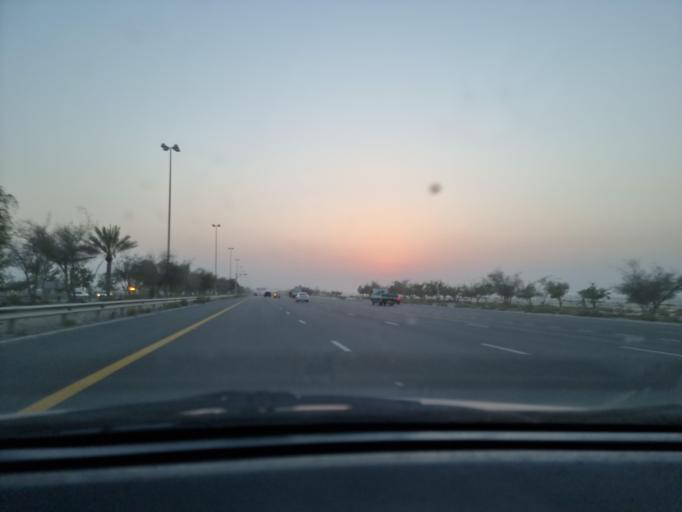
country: AE
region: Abu Dhabi
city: Abu Dhabi
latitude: 24.4135
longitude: 54.6986
